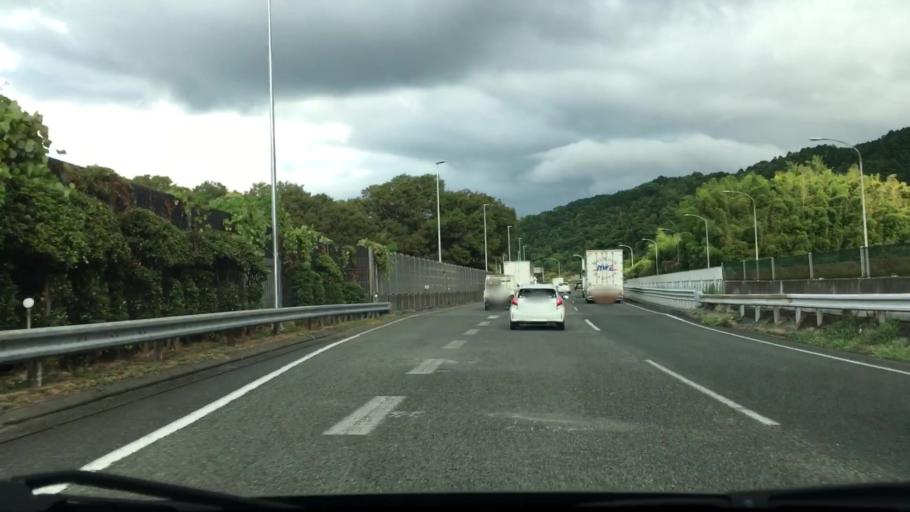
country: JP
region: Fukuoka
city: Nishifukuma
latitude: 33.7506
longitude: 130.5404
